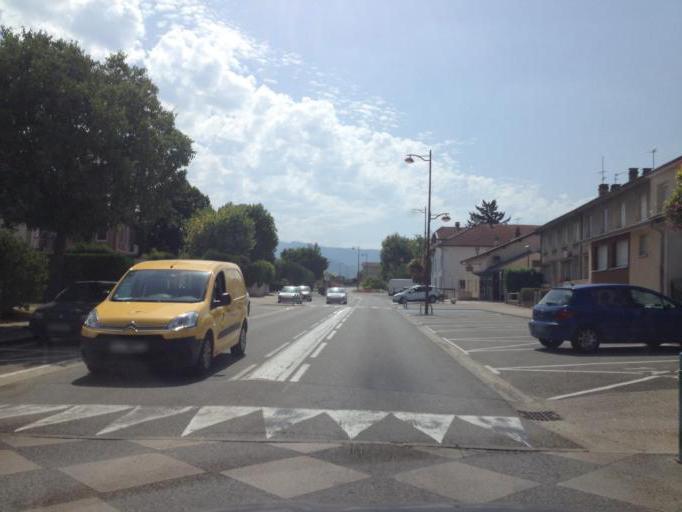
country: FR
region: Rhone-Alpes
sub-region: Departement de la Drome
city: Chatuzange-le-Goubet
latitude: 45.0057
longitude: 5.0912
